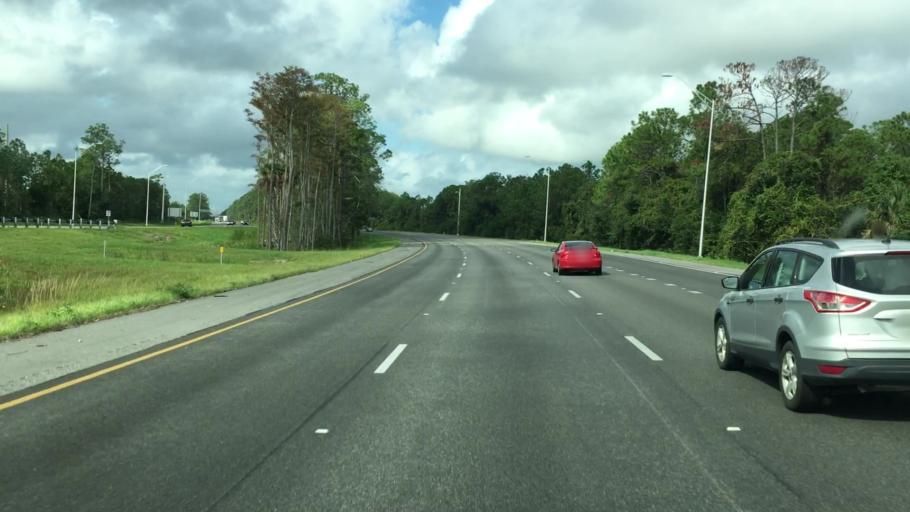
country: US
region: Florida
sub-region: Volusia County
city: Port Orange
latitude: 29.1125
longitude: -81.0322
